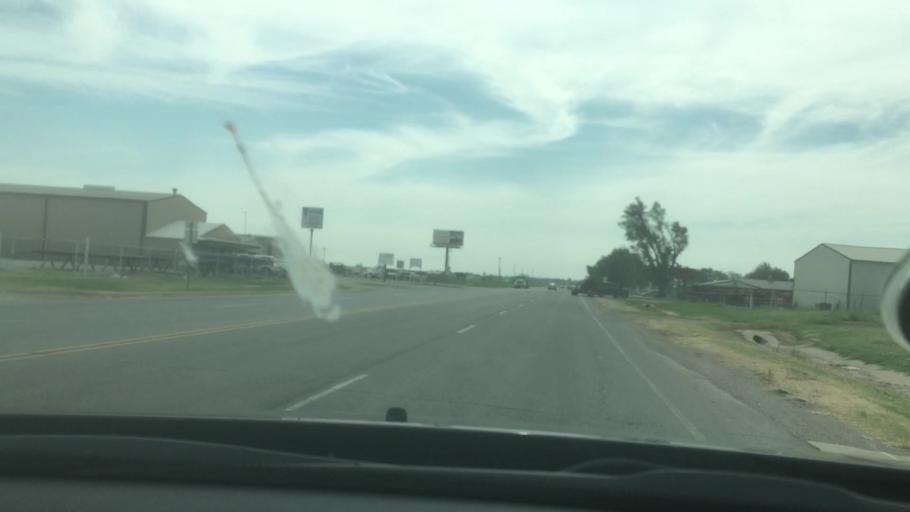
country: US
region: Oklahoma
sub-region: Garvin County
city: Lindsay
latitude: 34.8365
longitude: -97.5969
